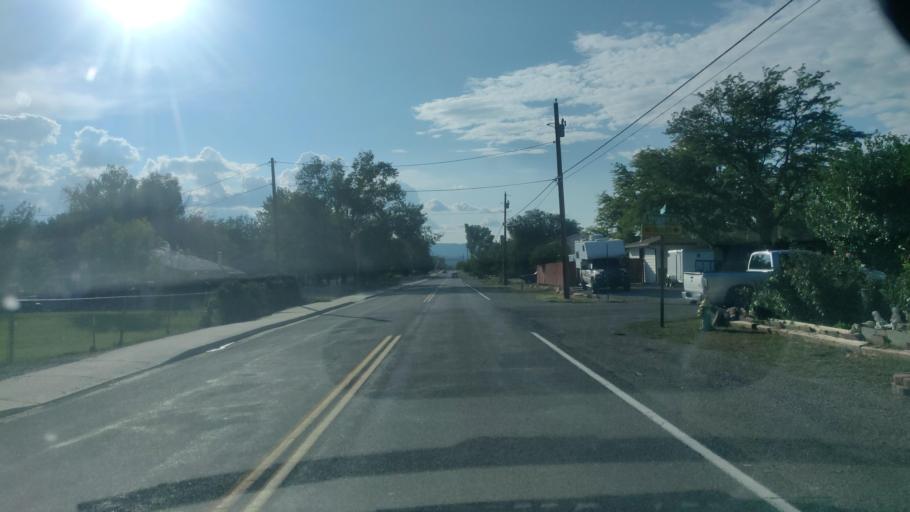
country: US
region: Colorado
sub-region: Mesa County
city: Orchard Mesa
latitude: 39.0340
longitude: -108.5098
